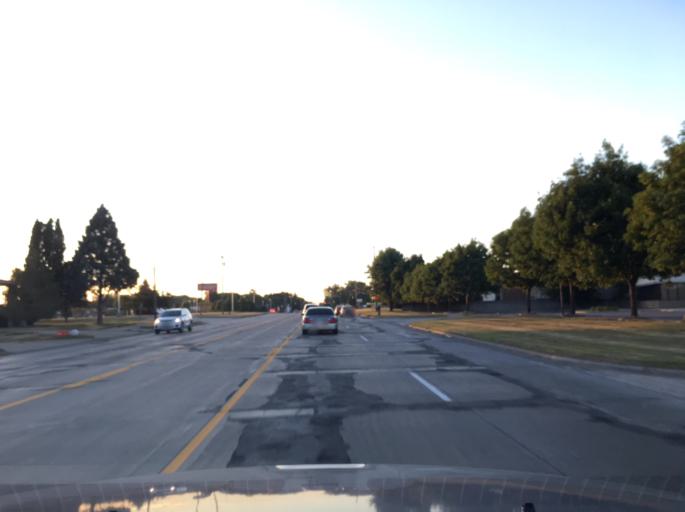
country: US
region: Michigan
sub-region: Macomb County
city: Fraser
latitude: 42.5502
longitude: -82.9593
